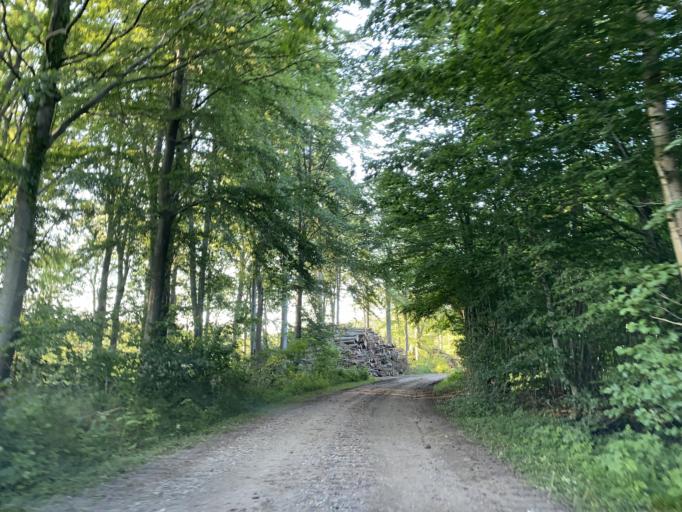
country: DK
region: South Denmark
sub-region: Haderslev Kommune
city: Starup
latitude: 55.1665
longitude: 9.5116
